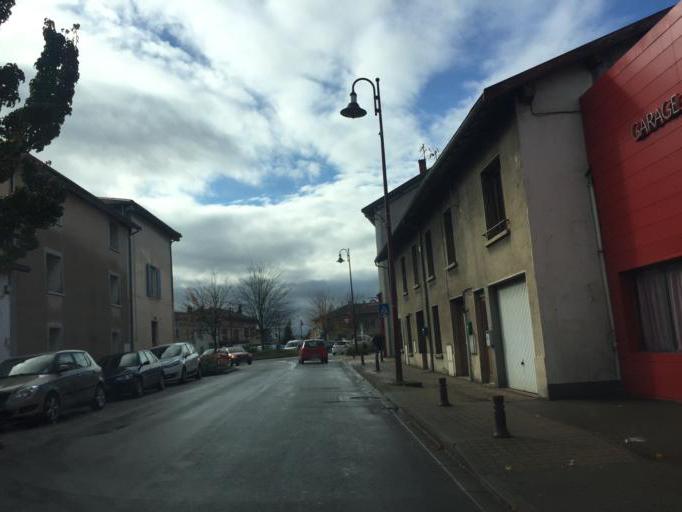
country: FR
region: Rhone-Alpes
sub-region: Departement de l'Ain
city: Saint-Andre-de-Corcy
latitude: 45.9267
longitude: 4.9518
